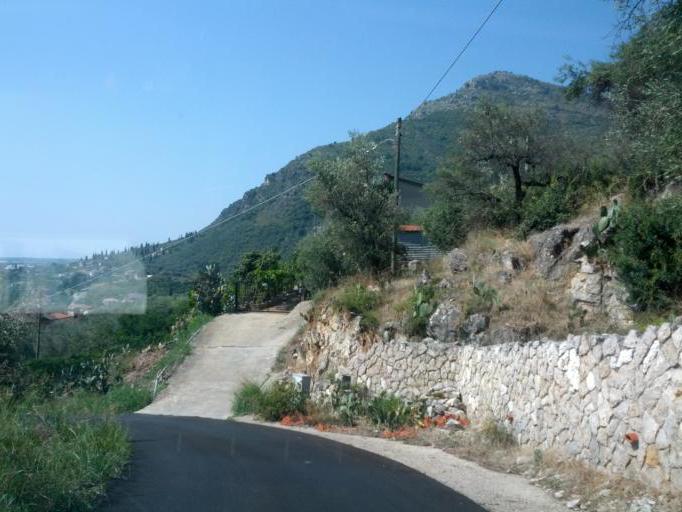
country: IT
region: Latium
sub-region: Provincia di Latina
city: Monte San Biagio
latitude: 41.3803
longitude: 13.3870
